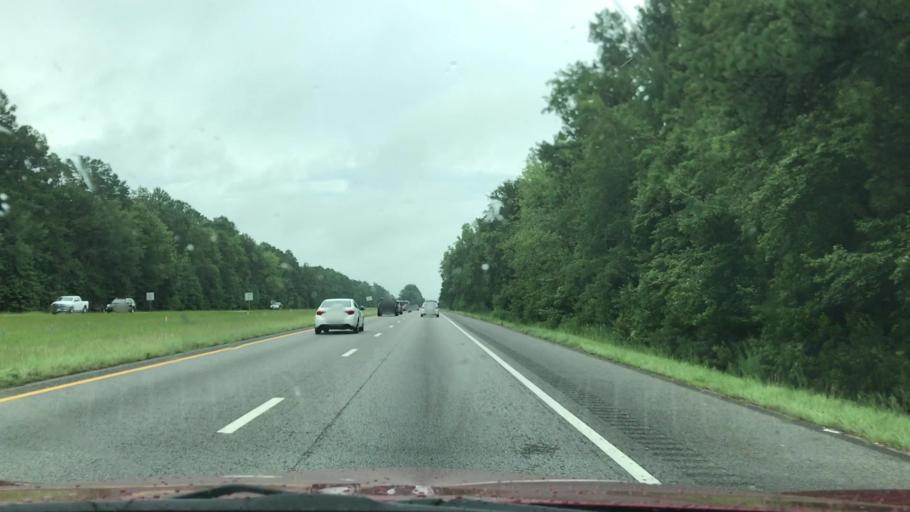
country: US
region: South Carolina
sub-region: Dorchester County
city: Ridgeville
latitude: 33.1802
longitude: -80.3774
